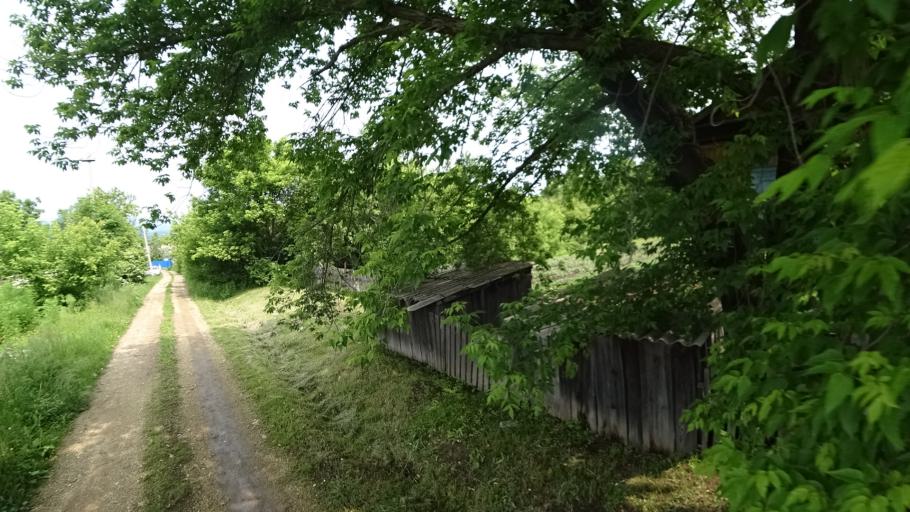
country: RU
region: Primorskiy
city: Novosysoyevka
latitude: 44.2534
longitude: 133.3778
